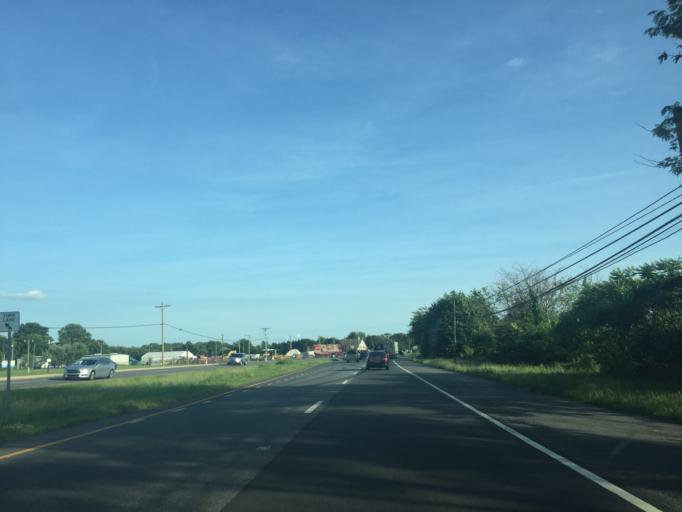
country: US
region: Delaware
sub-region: Kent County
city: Smyrna
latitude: 39.2658
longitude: -75.5874
